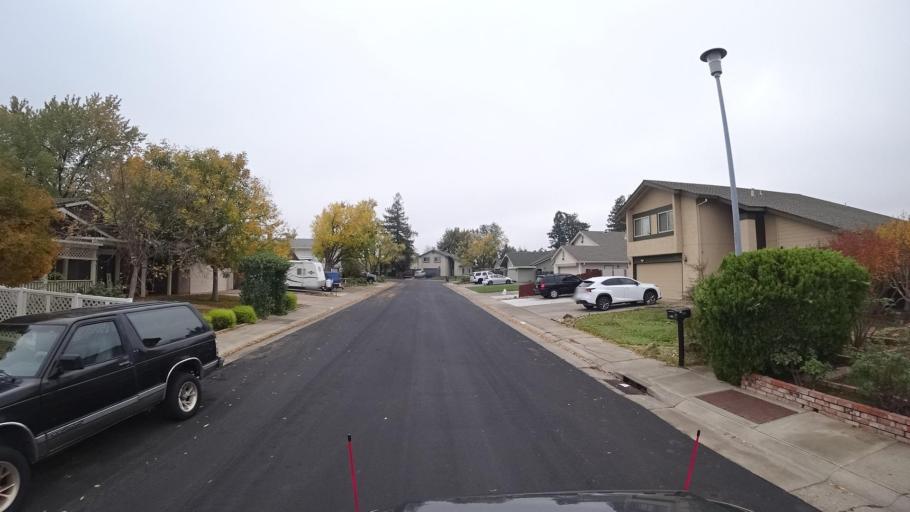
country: US
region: California
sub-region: Sacramento County
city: Elk Grove
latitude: 38.3956
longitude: -121.3635
